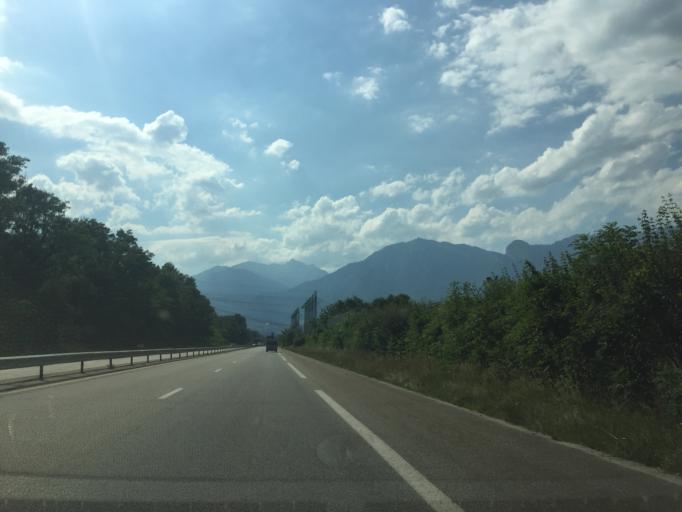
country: FR
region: Rhone-Alpes
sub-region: Departement de la Savoie
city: Albertville
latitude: 45.6594
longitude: 6.4247
